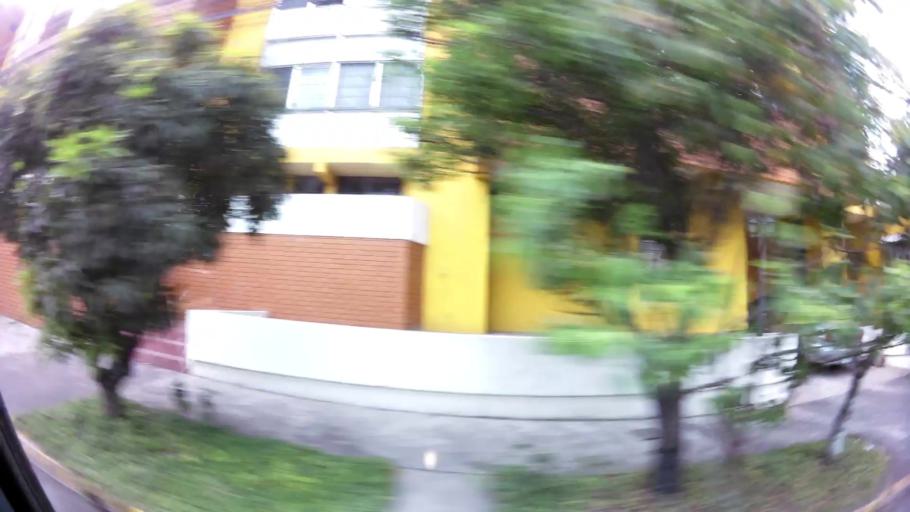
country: HN
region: Francisco Morazan
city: Tegucigalpa
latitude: 14.0978
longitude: -87.1858
